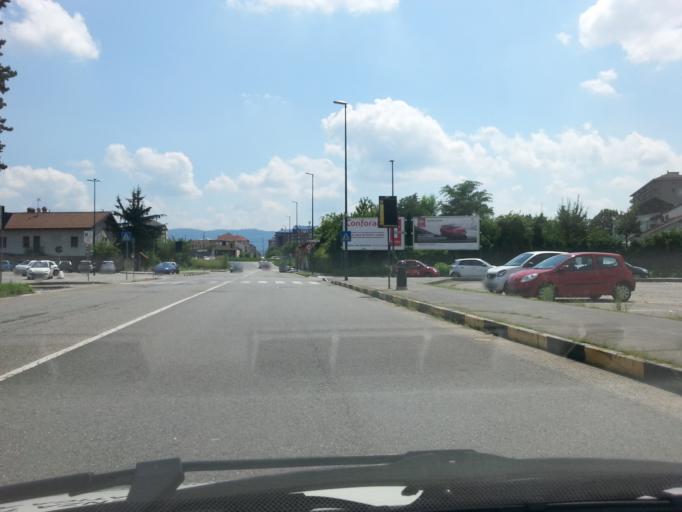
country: IT
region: Piedmont
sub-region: Provincia di Torino
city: Turin
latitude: 45.1000
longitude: 7.6849
